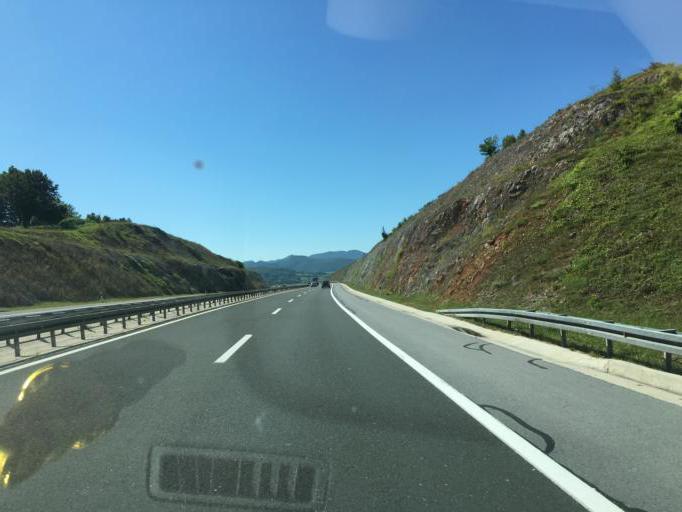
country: HR
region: Licko-Senjska
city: Otocac
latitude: 44.9174
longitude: 15.1695
